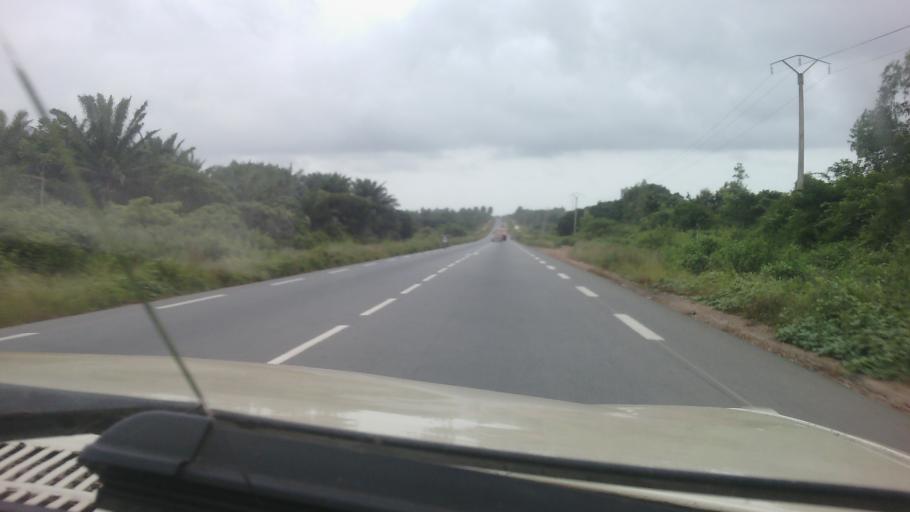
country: BJ
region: Atlantique
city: Ouidah
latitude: 6.3830
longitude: 2.0185
